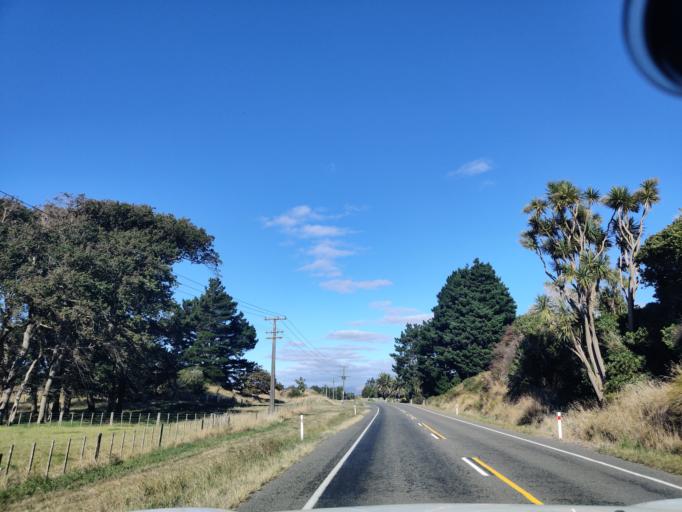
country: NZ
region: Manawatu-Wanganui
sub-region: Horowhenua District
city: Foxton
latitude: -40.4099
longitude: 175.3809
